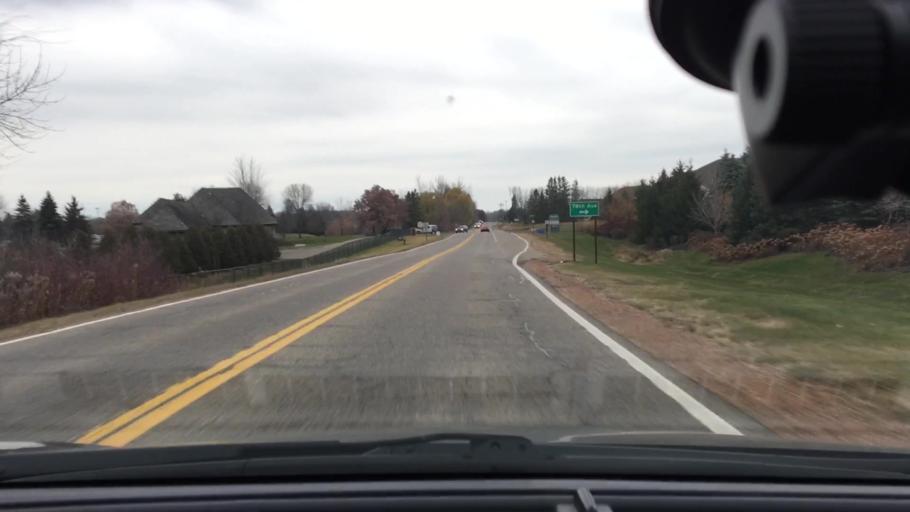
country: US
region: Minnesota
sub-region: Hennepin County
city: Corcoran
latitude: 45.0948
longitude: -93.5125
